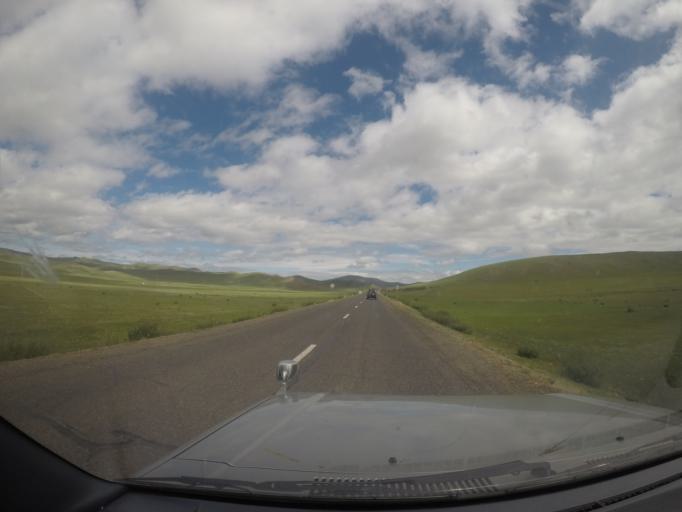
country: MN
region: Hentiy
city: Modot
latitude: 47.7443
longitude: 108.9893
